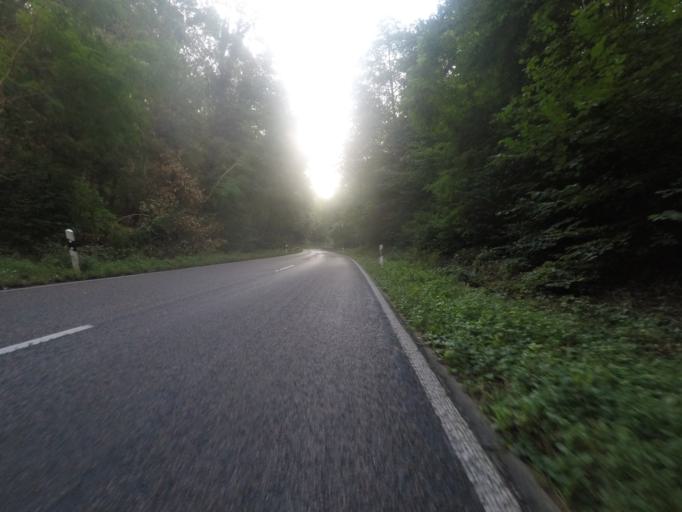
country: DE
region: Baden-Wuerttemberg
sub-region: Karlsruhe Region
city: Ettlingen
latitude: 48.9158
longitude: 8.3976
